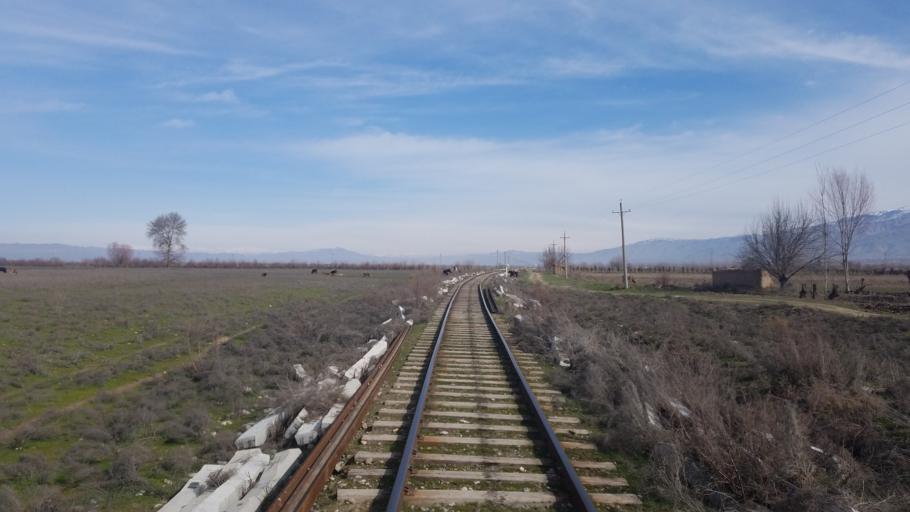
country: TJ
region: Khatlon
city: Abdurahmoni Jomi
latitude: 38.0435
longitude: 68.8500
